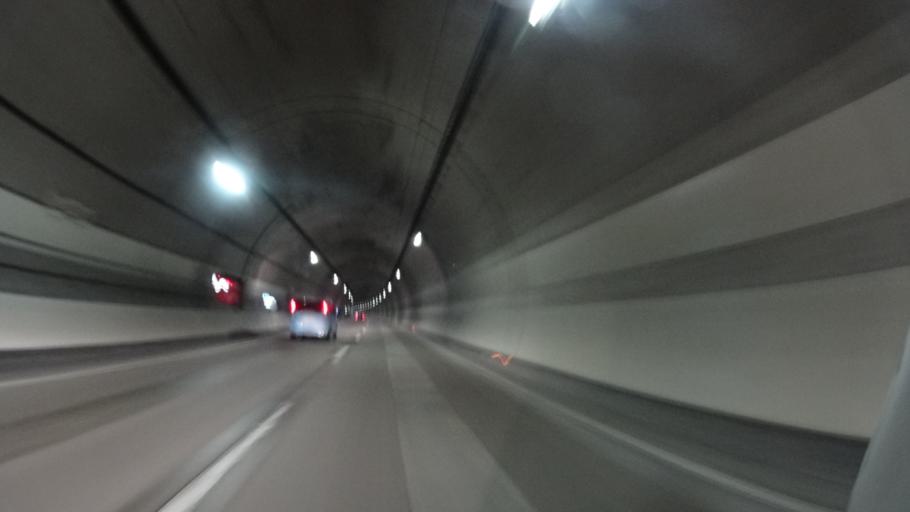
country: JP
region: Kyoto
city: Kyoto
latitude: 34.9724
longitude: 135.7815
